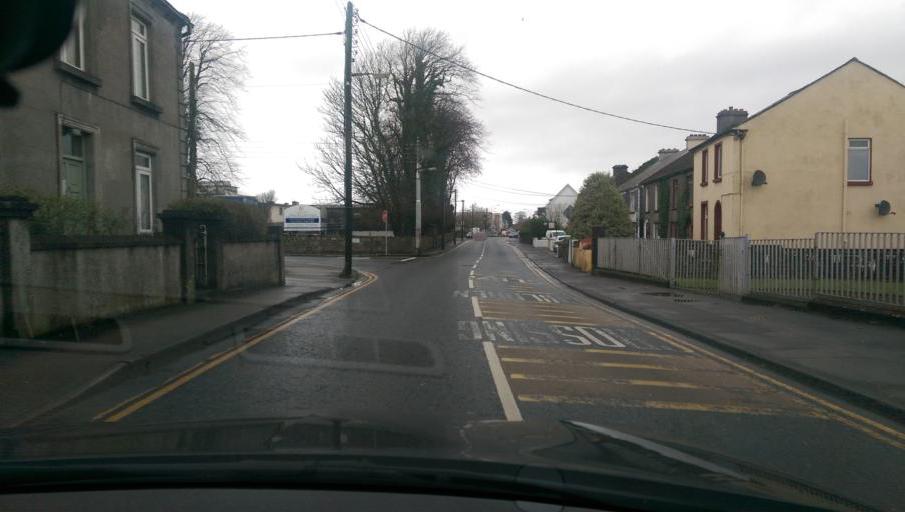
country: IE
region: Connaught
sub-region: County Galway
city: Gaillimh
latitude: 53.2743
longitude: -9.0631
